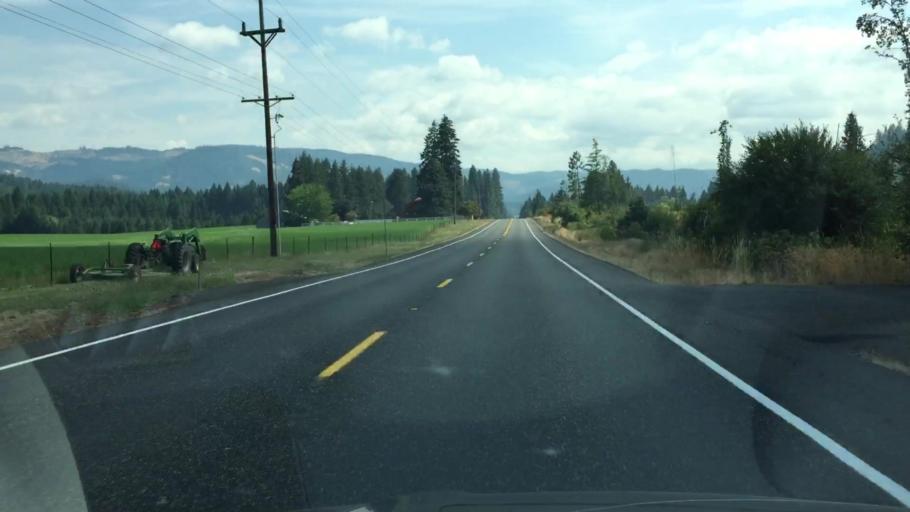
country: US
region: Washington
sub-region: Klickitat County
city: White Salmon
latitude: 45.8442
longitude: -121.5050
